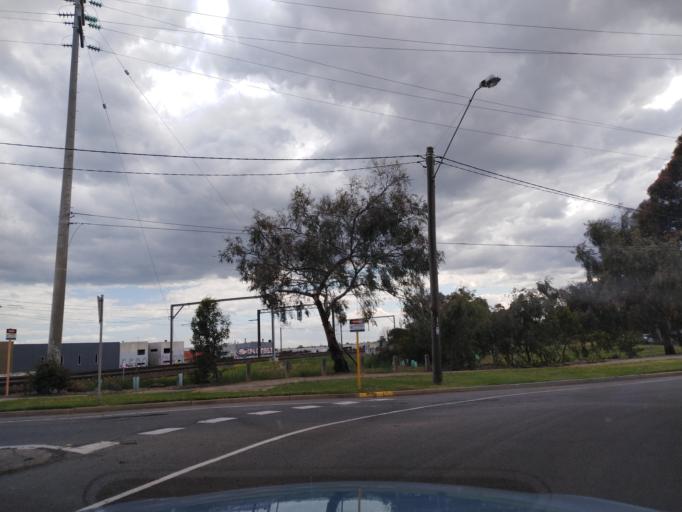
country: AU
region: Victoria
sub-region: Hobsons Bay
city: Williamstown North
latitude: -37.8488
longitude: 144.8745
